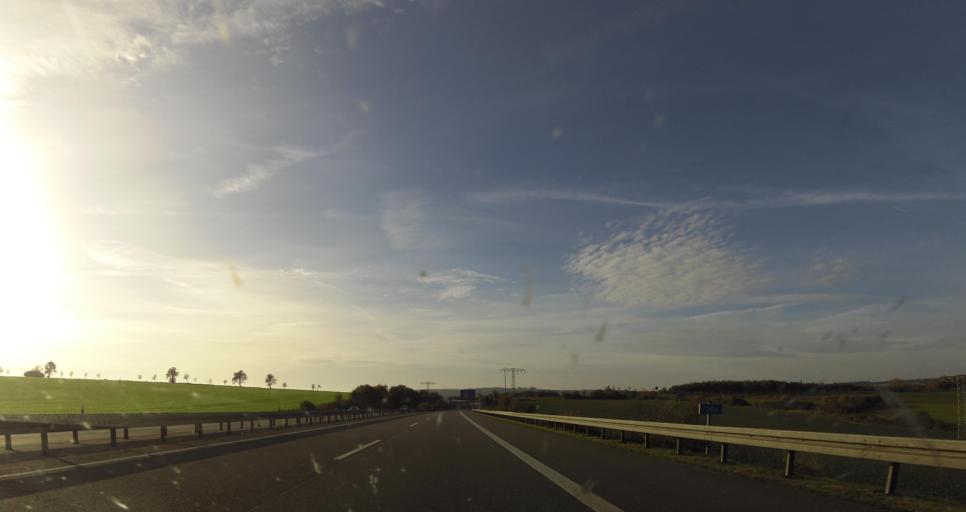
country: DE
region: Thuringia
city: Hausen
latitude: 51.3969
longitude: 10.3524
